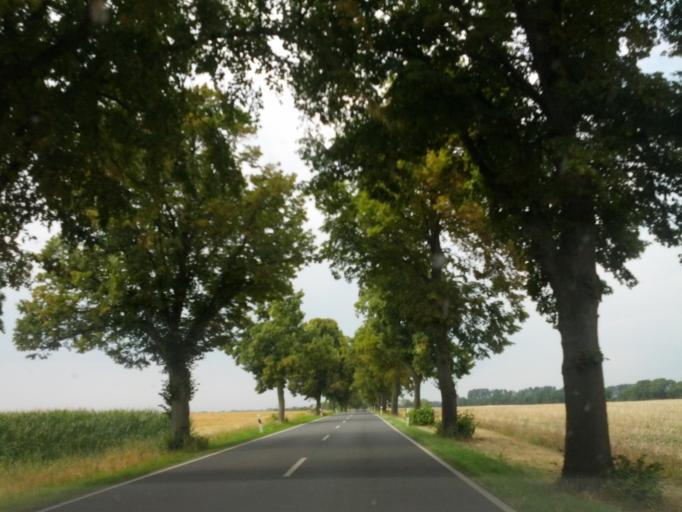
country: DE
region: Brandenburg
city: Fehrbellin
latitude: 52.7805
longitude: 12.8285
